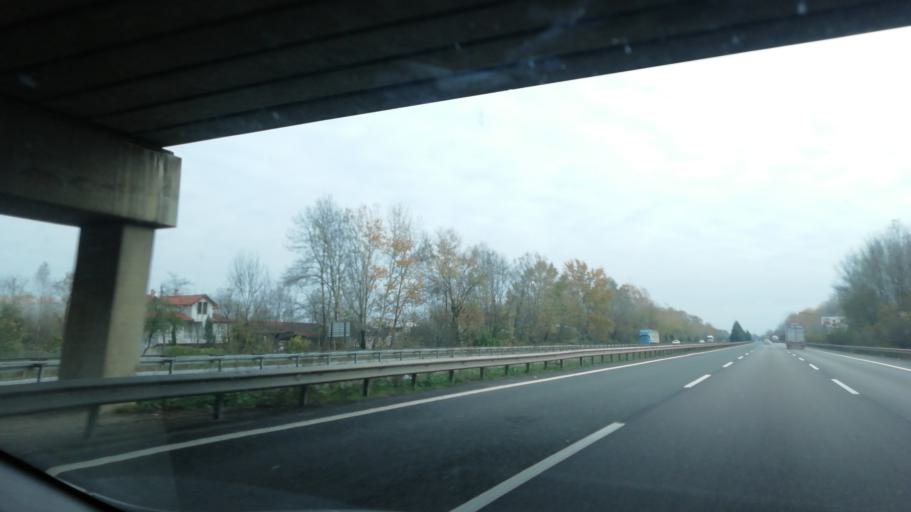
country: TR
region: Sakarya
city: Akyazi
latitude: 40.7213
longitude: 30.6066
